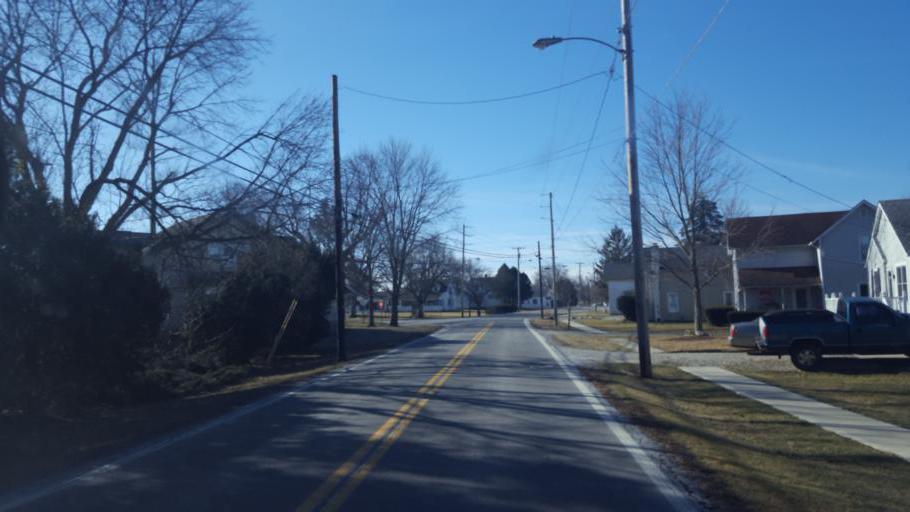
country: US
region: Ohio
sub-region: Marion County
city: Prospect
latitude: 40.5341
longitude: -83.2088
